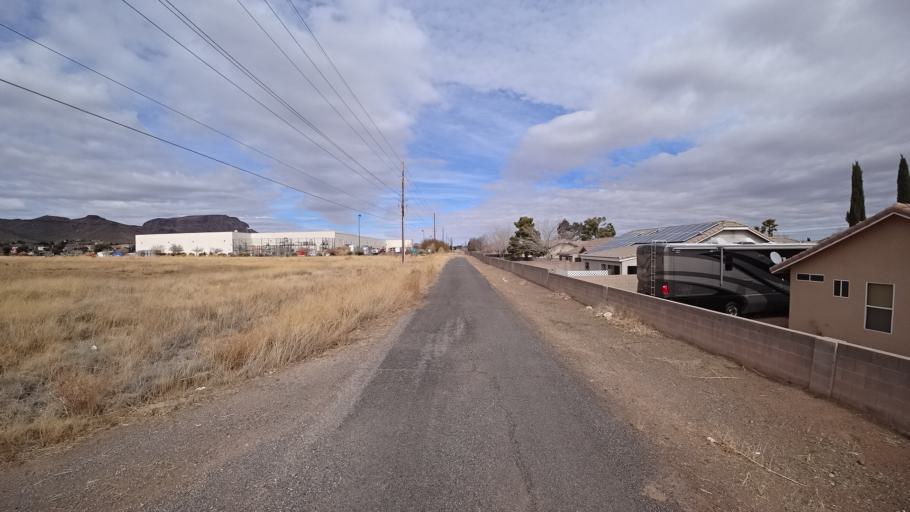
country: US
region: Arizona
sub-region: Mohave County
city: New Kingman-Butler
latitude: 35.2331
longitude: -114.0336
